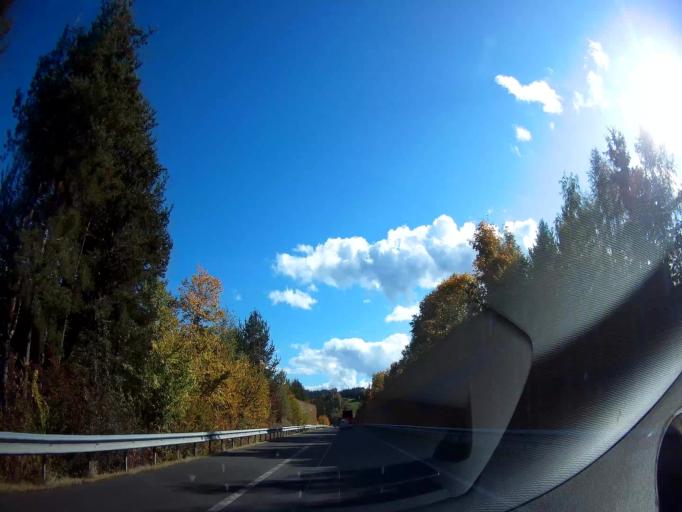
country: AT
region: Carinthia
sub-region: Politischer Bezirk Spittal an der Drau
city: Spittal an der Drau
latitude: 46.8242
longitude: 13.4849
